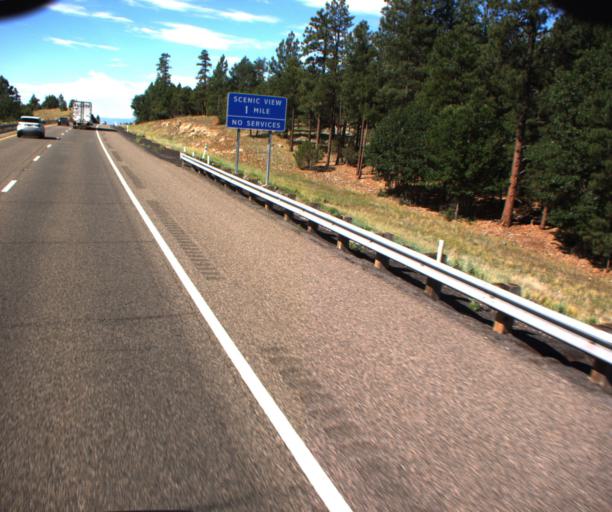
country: US
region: Arizona
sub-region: Coconino County
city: Sedona
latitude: 34.8296
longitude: -111.6080
